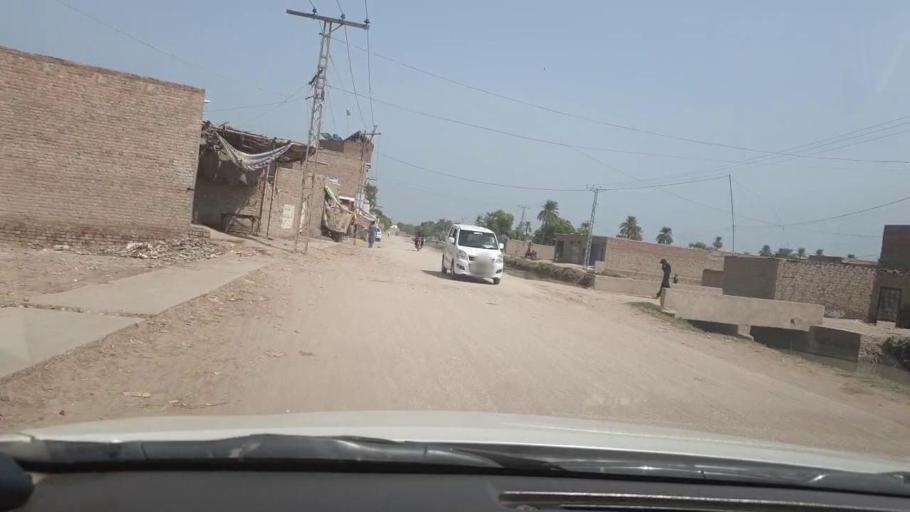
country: PK
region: Sindh
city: Shikarpur
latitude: 27.9444
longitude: 68.6341
